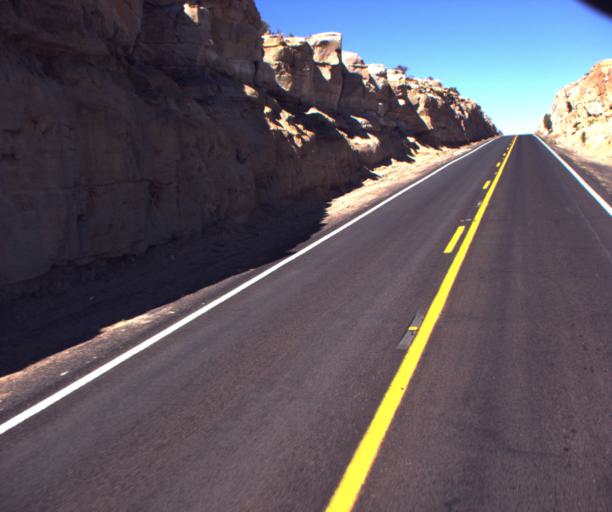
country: US
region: Arizona
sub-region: Navajo County
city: First Mesa
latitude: 35.9006
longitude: -110.6651
